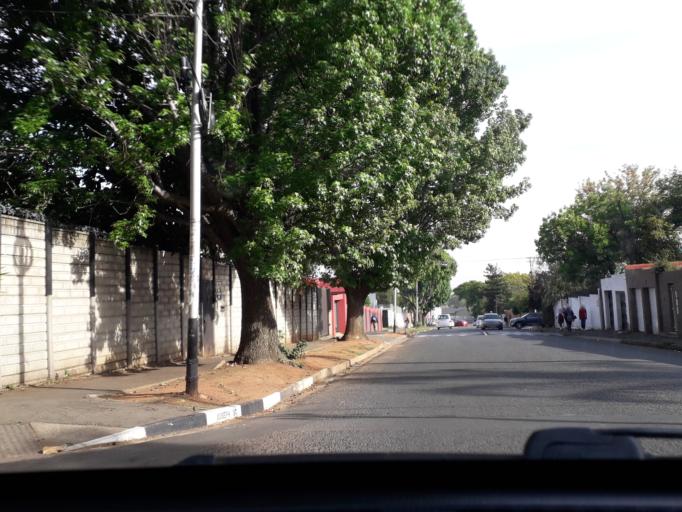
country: ZA
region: Gauteng
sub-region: City of Johannesburg Metropolitan Municipality
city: Johannesburg
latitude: -26.1413
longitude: 28.0888
